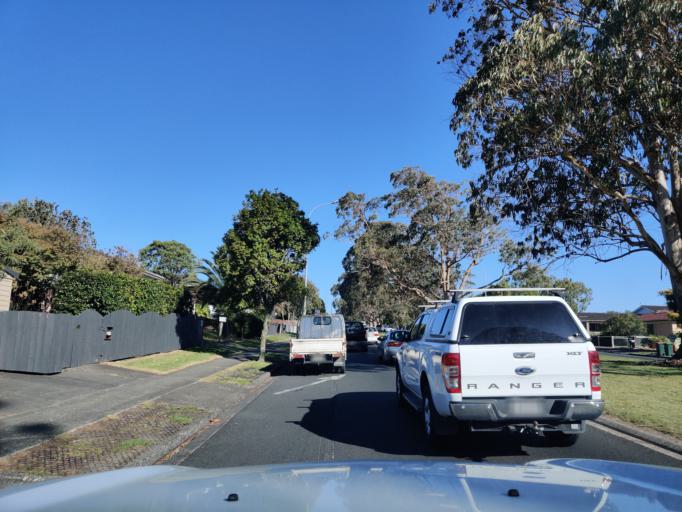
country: NZ
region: Auckland
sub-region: Auckland
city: Wiri
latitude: -37.0227
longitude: 174.8643
